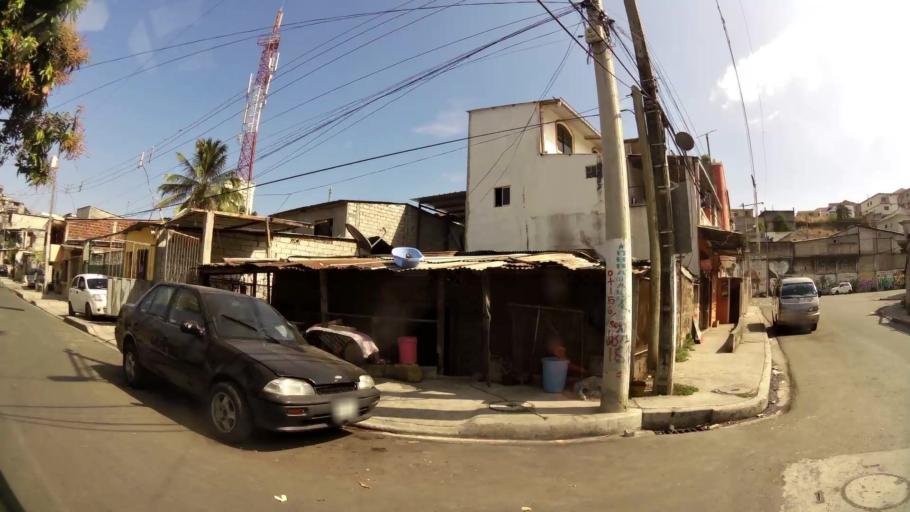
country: EC
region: Guayas
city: Guayaquil
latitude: -2.1508
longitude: -79.9404
